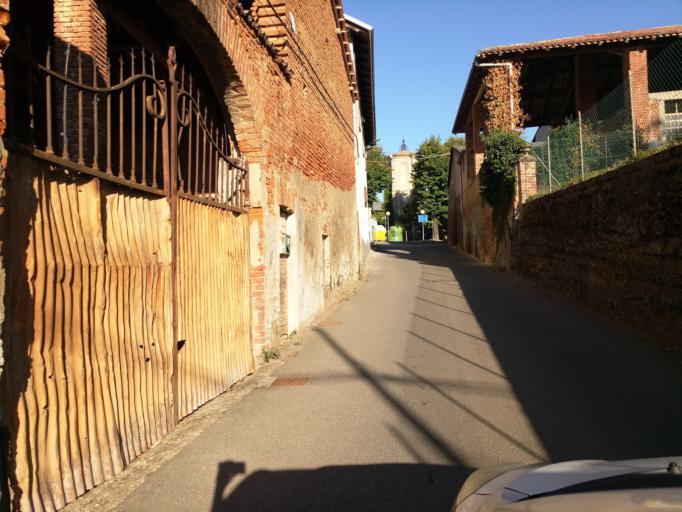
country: IT
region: Piedmont
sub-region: Provincia di Alessandria
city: Pomaro Monferrato
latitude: 45.0560
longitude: 8.6071
